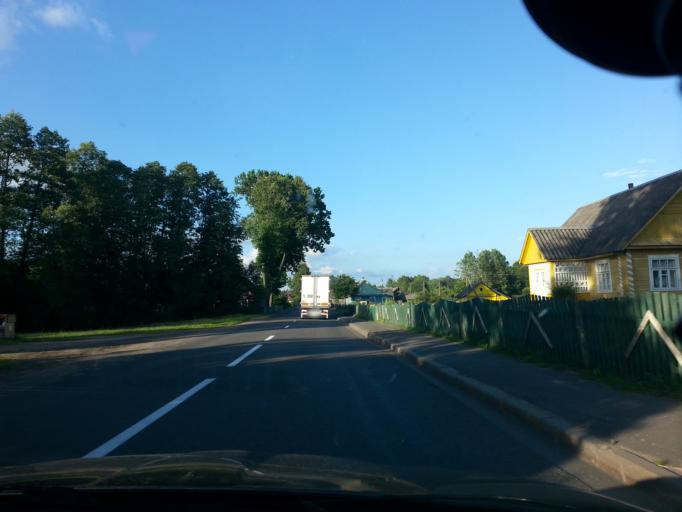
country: BY
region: Minsk
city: Svir
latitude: 54.9164
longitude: 26.4515
